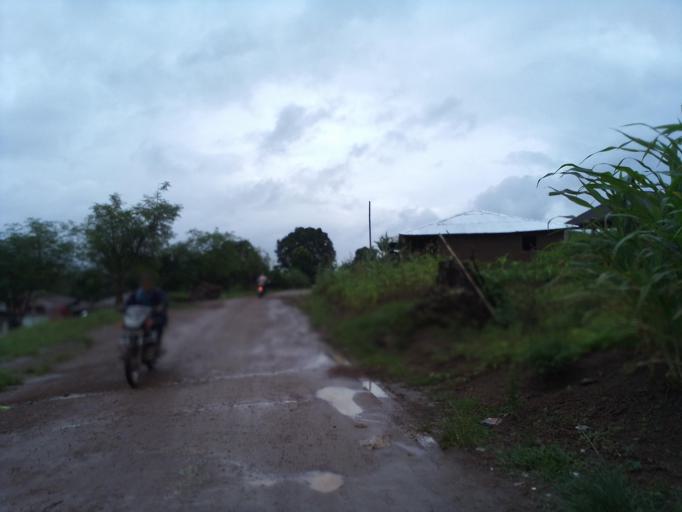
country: SL
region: Eastern Province
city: Kenema
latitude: 7.8804
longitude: -11.1574
